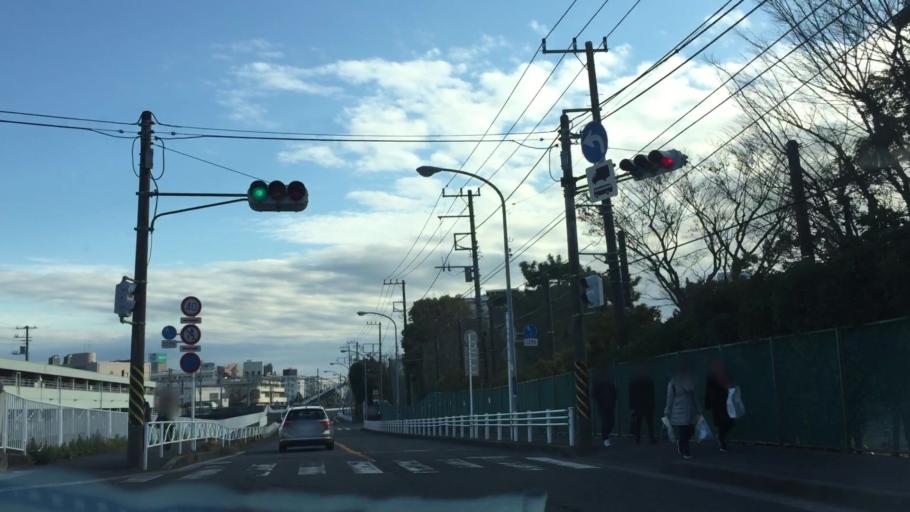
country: JP
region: Kanagawa
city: Zushi
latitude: 35.3412
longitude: 139.6194
